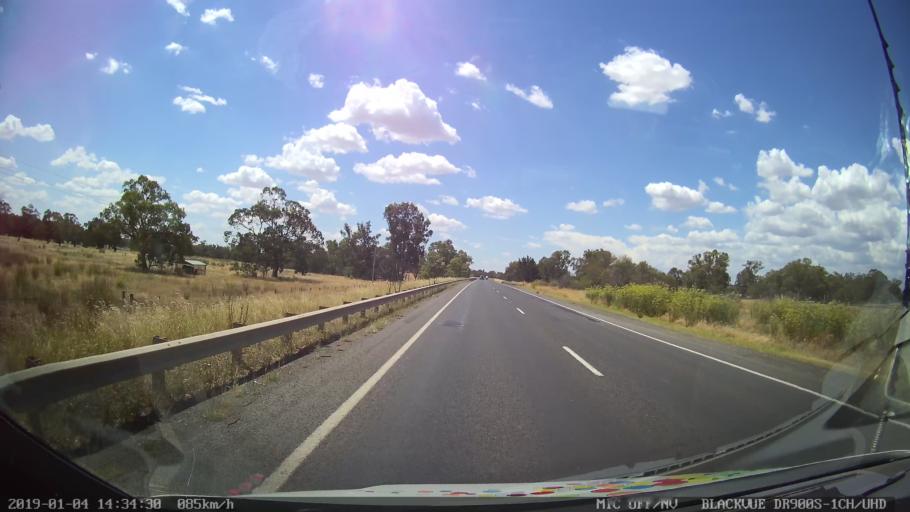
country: AU
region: New South Wales
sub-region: Dubbo Municipality
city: Dubbo
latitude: -32.1977
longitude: 148.6205
